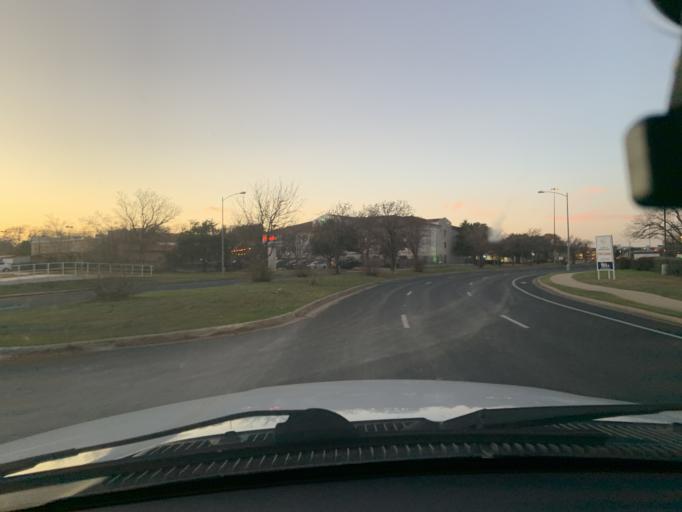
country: US
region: Texas
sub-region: Williamson County
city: Anderson Mill
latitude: 30.4639
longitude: -97.8028
